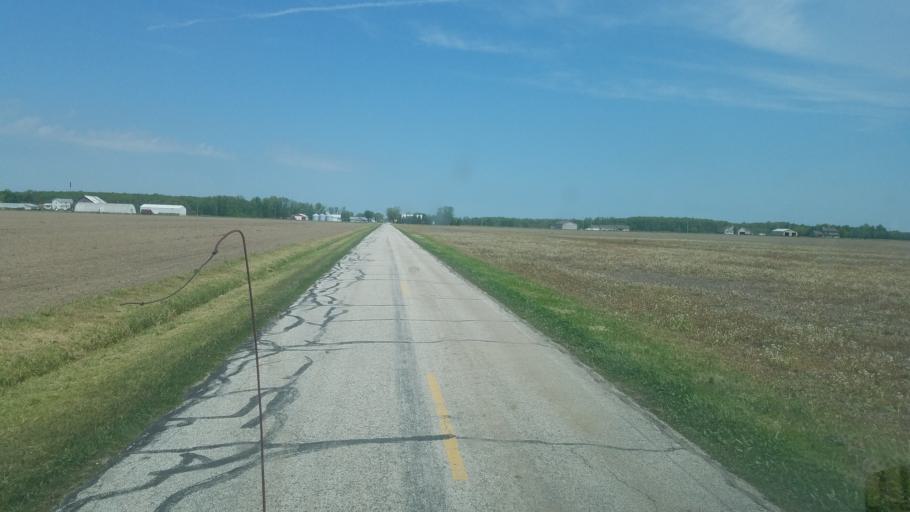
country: US
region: Ohio
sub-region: Ottawa County
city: Oak Harbor
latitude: 41.4676
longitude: -83.2017
